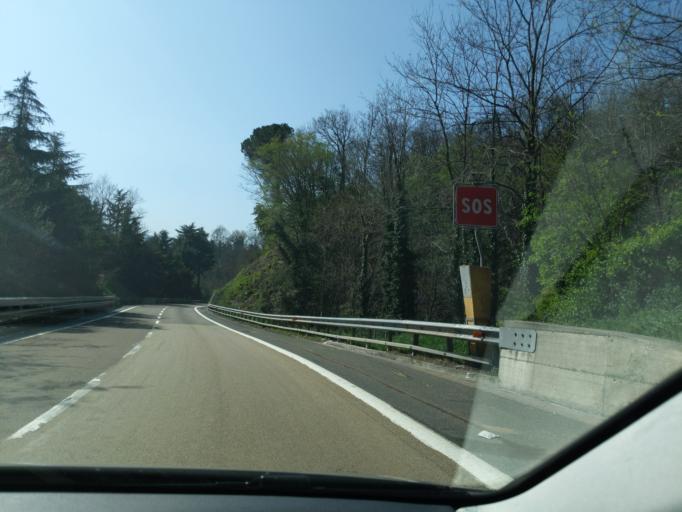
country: IT
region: Liguria
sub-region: Provincia di Genova
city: Pedemonte
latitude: 44.4909
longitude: 8.9192
